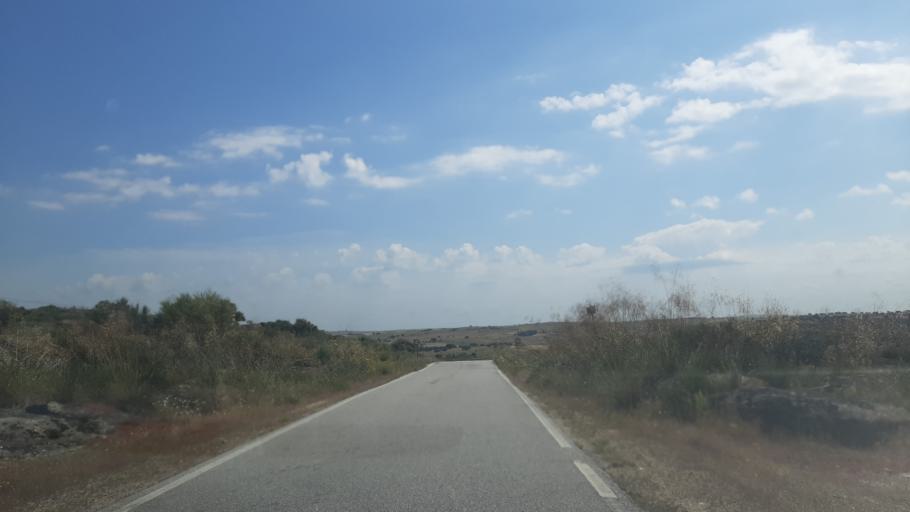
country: ES
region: Castille and Leon
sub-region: Provincia de Salamanca
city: Fuentes de Onoro
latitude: 40.6447
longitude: -6.7851
